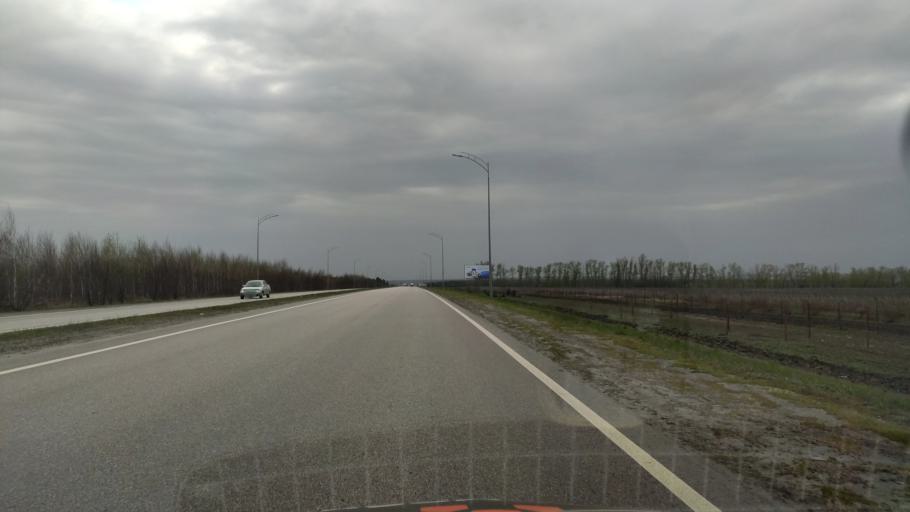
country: RU
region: Belgorod
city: Staryy Oskol
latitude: 51.3794
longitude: 37.8529
